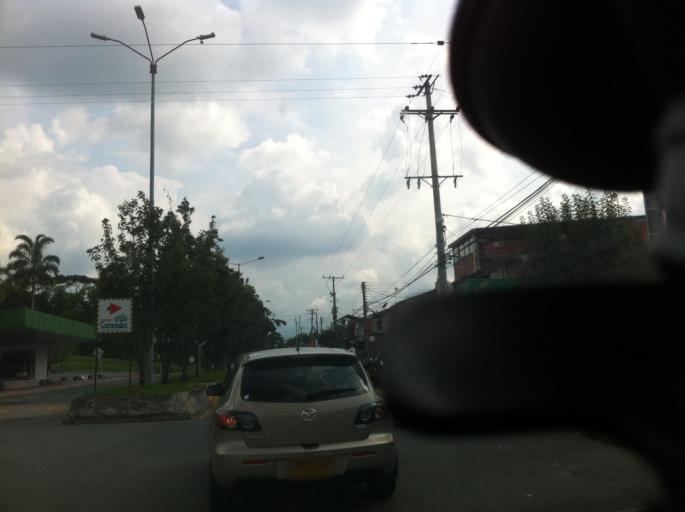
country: CO
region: Quindio
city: Armenia
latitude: 4.5148
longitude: -75.7021
